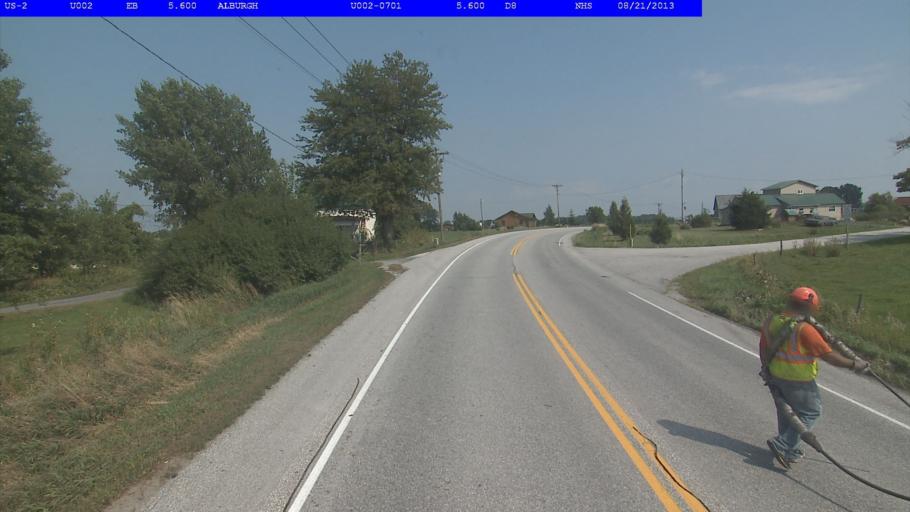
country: US
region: New York
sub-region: Clinton County
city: Rouses Point
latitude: 44.9653
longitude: -73.2867
